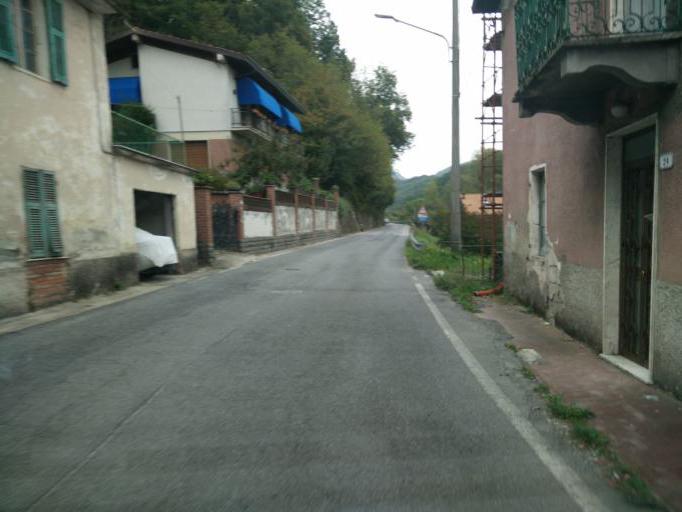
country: IT
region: Tuscany
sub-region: Provincia di Massa-Carrara
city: Fivizzano
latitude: 44.1954
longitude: 10.1115
